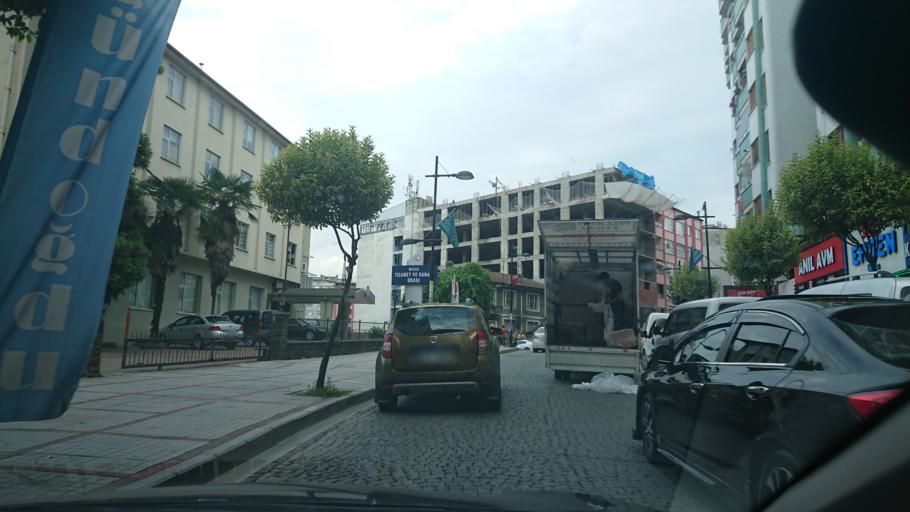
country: TR
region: Rize
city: Rize
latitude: 41.0246
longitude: 40.5241
